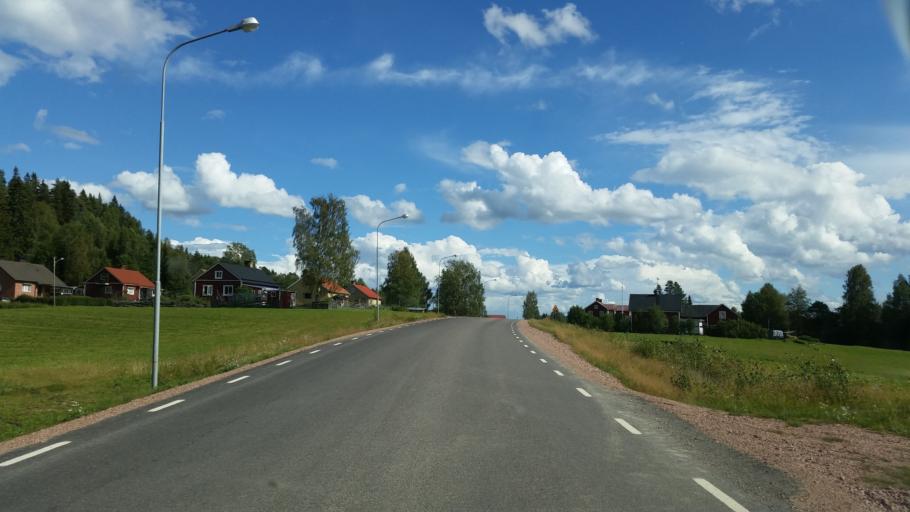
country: SE
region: Gaevleborg
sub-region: Ljusdals Kommun
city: Ljusdal
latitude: 61.9733
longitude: 16.3326
